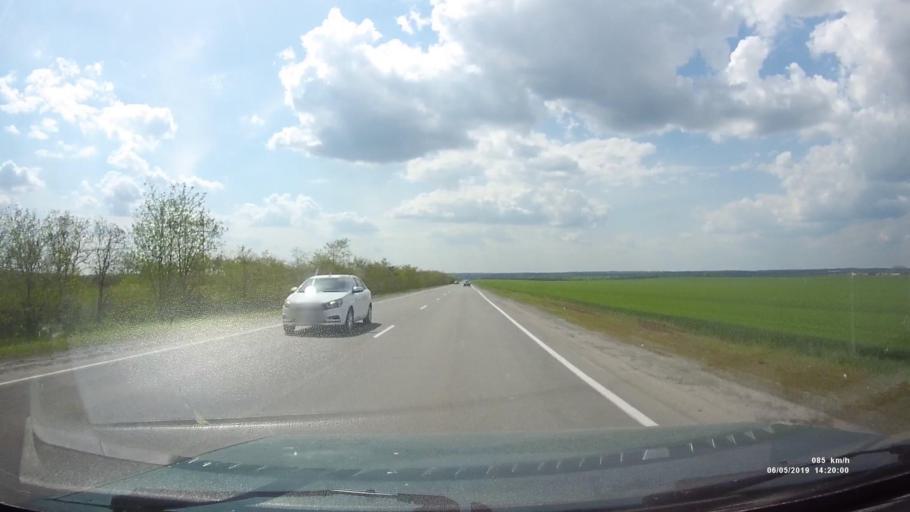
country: RU
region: Rostov
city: Kamenolomni
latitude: 47.6325
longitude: 40.2215
